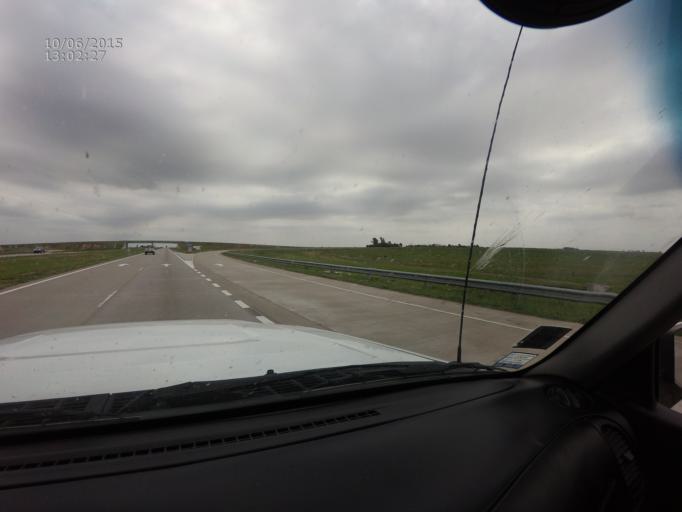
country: AR
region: Santa Fe
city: Armstrong
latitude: -32.7859
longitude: -61.7418
